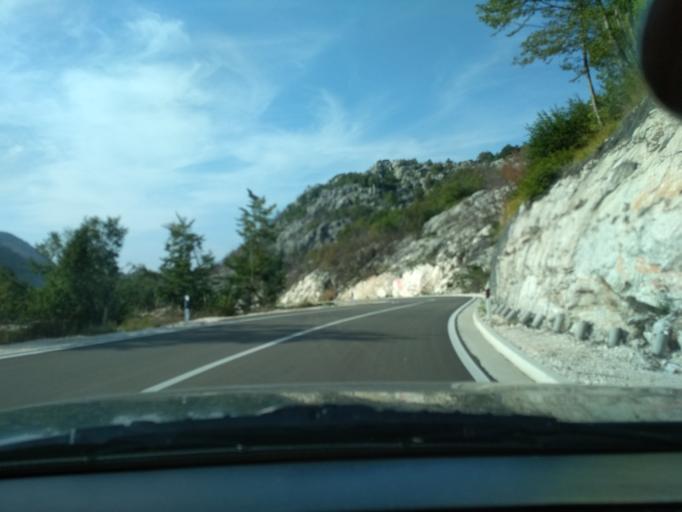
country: ME
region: Cetinje
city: Cetinje
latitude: 42.4285
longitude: 18.8650
